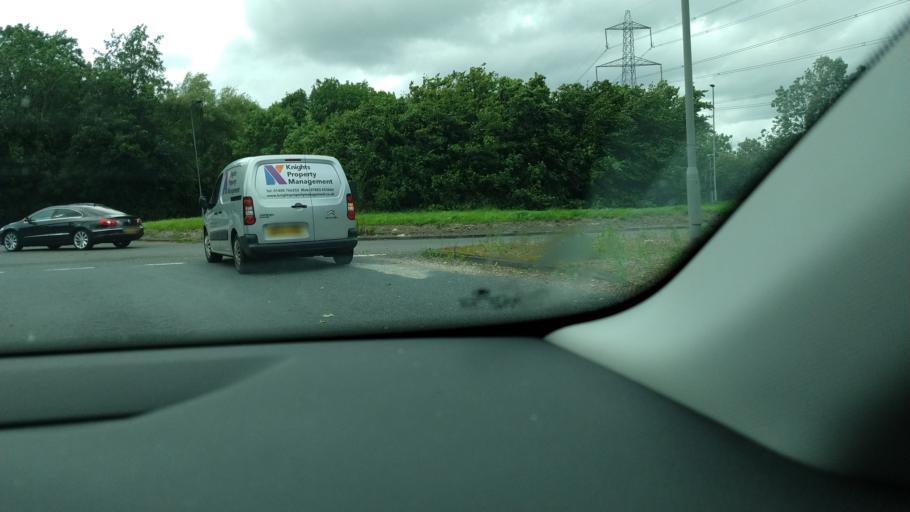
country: GB
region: England
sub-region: North Yorkshire
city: Camblesforth
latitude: 53.7294
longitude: -0.9925
